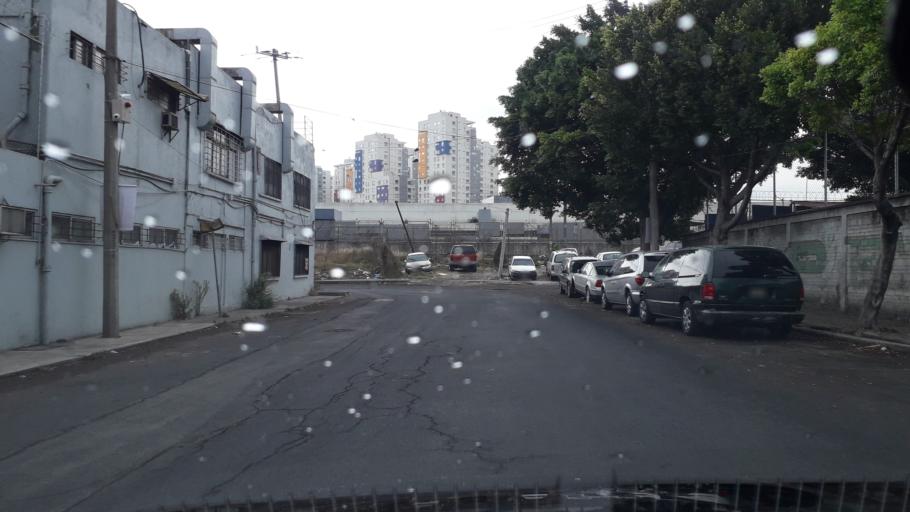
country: MX
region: Mexico City
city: Cuauhtemoc
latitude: 19.4621
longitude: -99.1581
